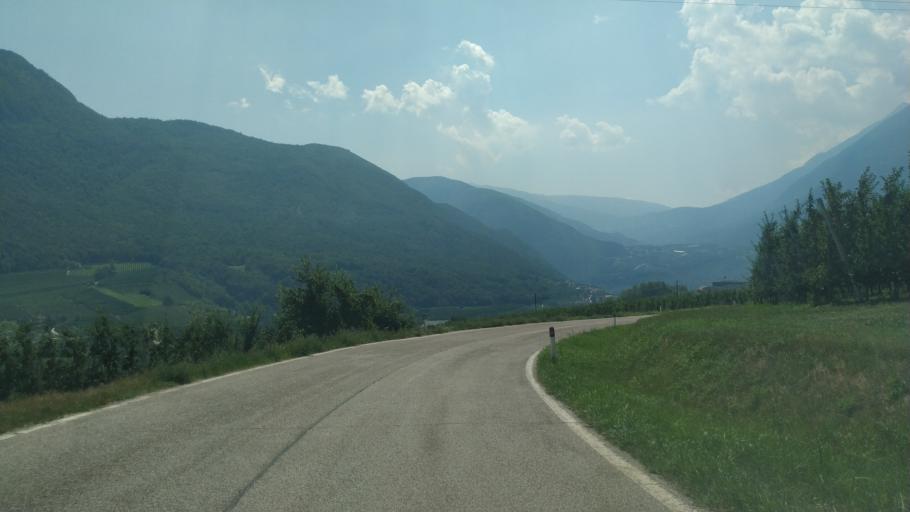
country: IT
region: Trentino-Alto Adige
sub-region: Provincia di Trento
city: Vigo di Ton
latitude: 46.2647
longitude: 11.0779
